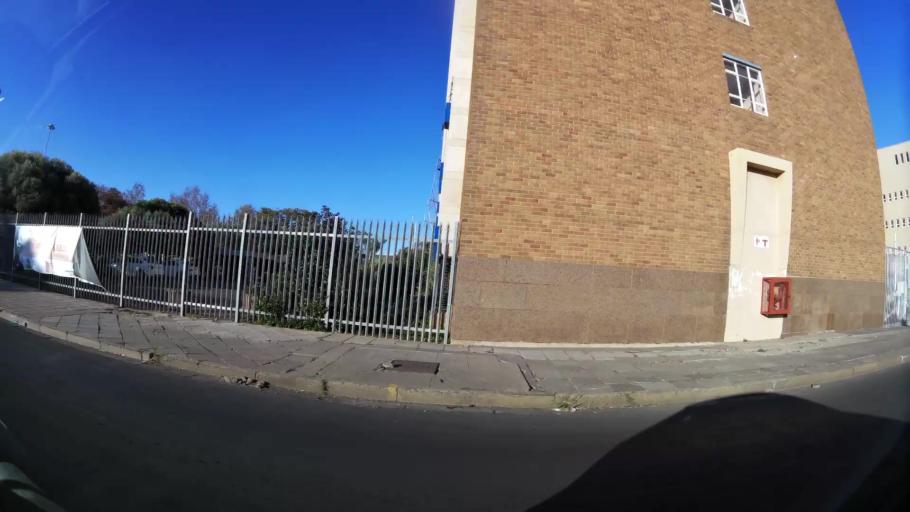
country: ZA
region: Northern Cape
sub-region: Frances Baard District Municipality
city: Kimberley
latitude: -28.7362
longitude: 24.7687
